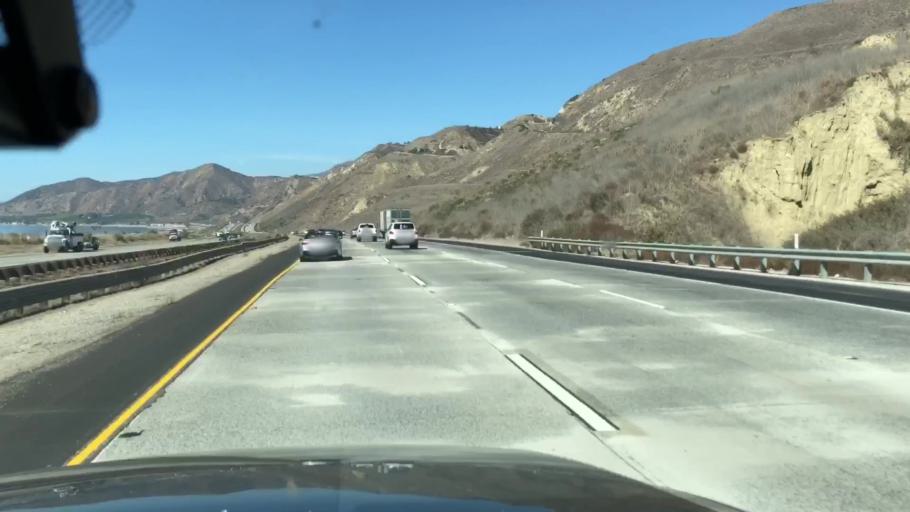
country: US
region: California
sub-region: Ventura County
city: Ventura
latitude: 34.3062
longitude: -119.3486
